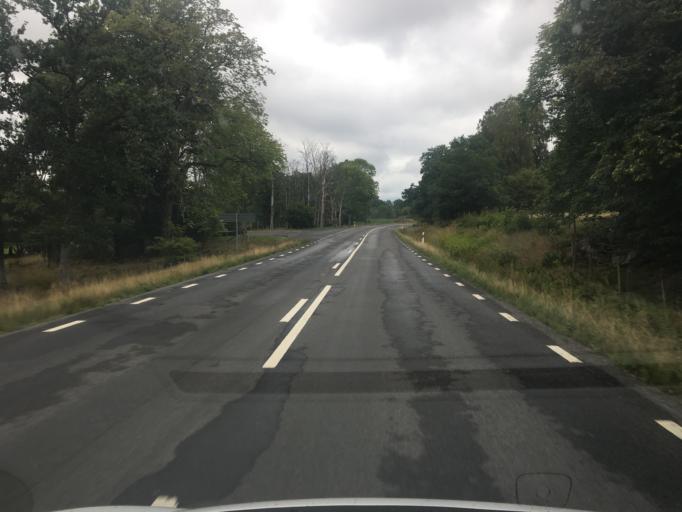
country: SE
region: Kronoberg
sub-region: Ljungby Kommun
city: Lagan
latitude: 57.0296
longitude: 14.0213
